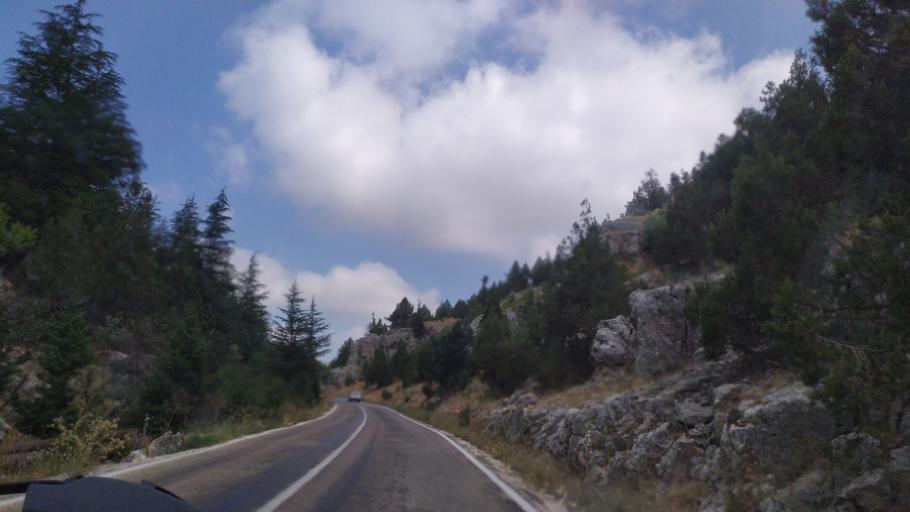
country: TR
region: Mersin
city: Kirobasi
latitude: 36.6111
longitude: 33.8812
